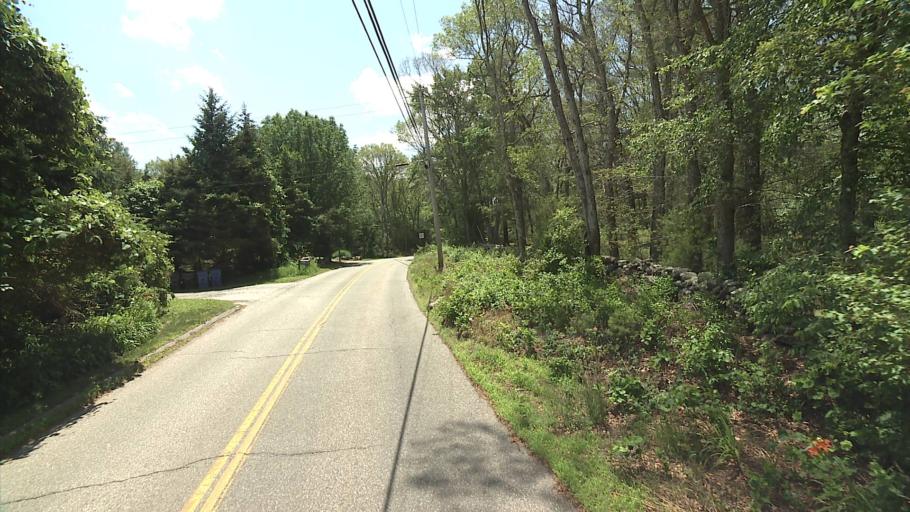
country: US
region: Connecticut
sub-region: New London County
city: Preston City
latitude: 41.5341
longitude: -71.8801
